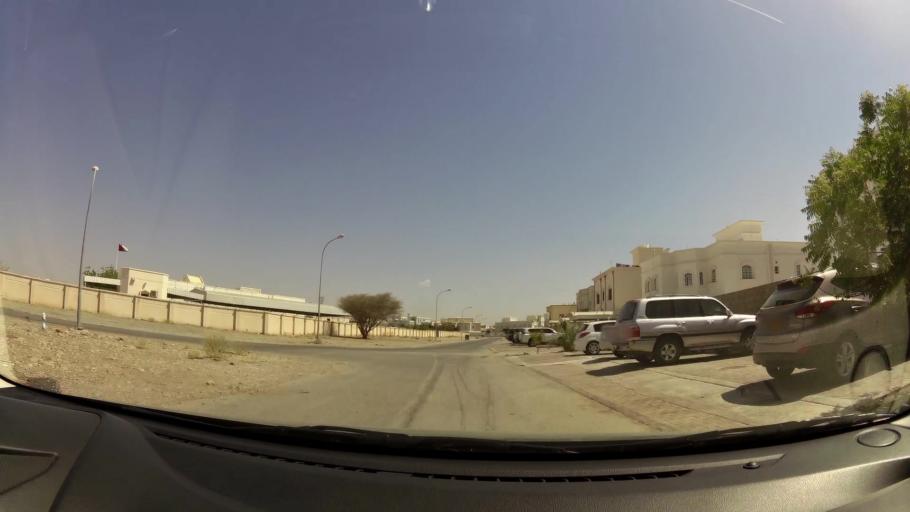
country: OM
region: Muhafazat Masqat
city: As Sib al Jadidah
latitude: 23.6245
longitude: 58.2161
